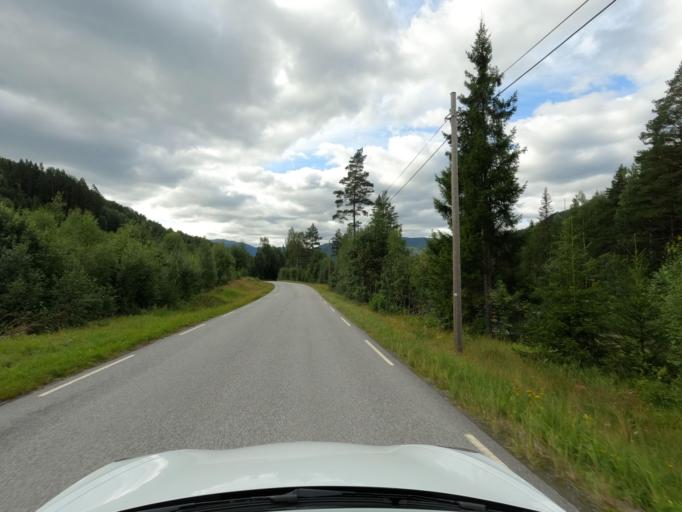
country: NO
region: Telemark
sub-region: Tinn
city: Rjukan
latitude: 60.0087
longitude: 8.8352
